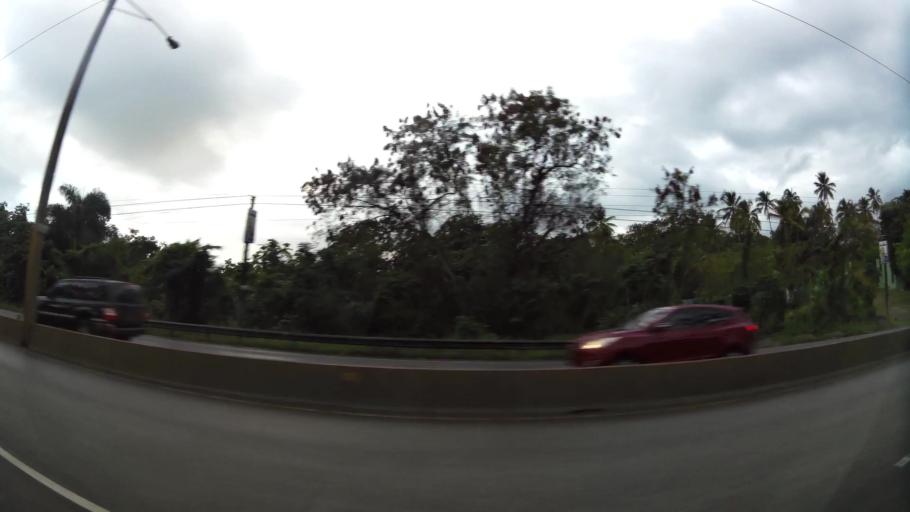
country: DO
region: San Cristobal
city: Villa Altagracia
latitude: 18.5741
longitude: -70.1043
